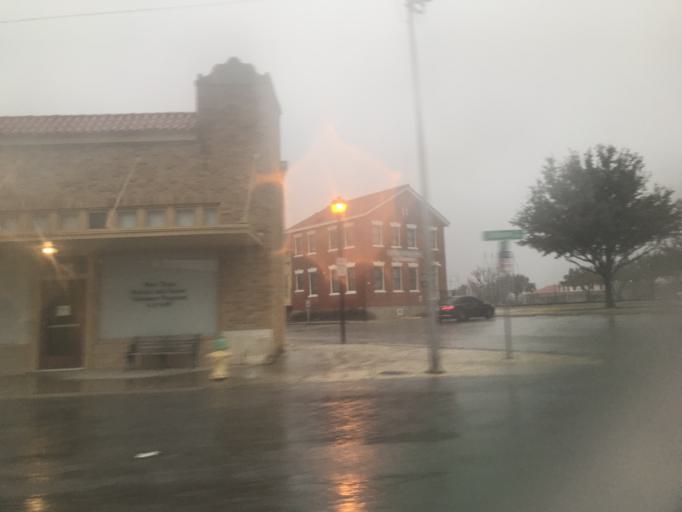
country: US
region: Texas
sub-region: Tom Green County
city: San Angelo
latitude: 31.4545
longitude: -100.4346
